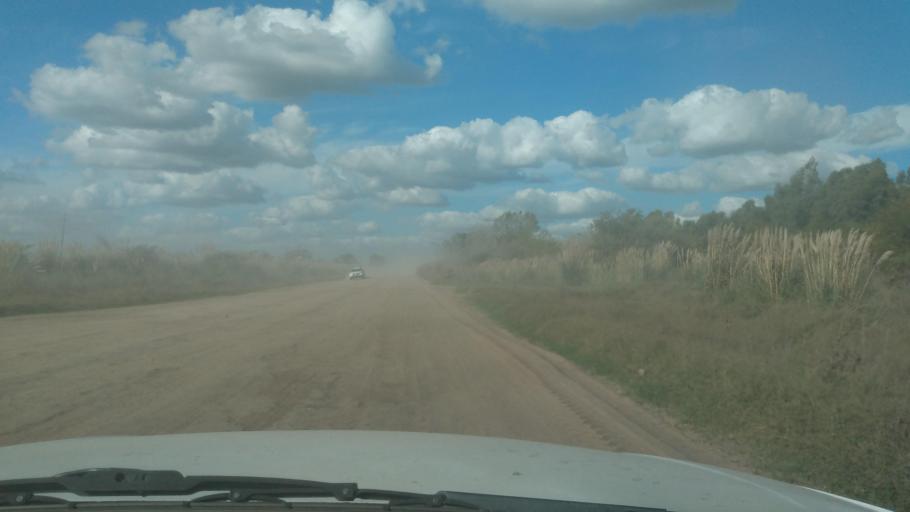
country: AR
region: Buenos Aires
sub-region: Partido de Navarro
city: Navarro
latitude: -35.0080
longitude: -59.3944
